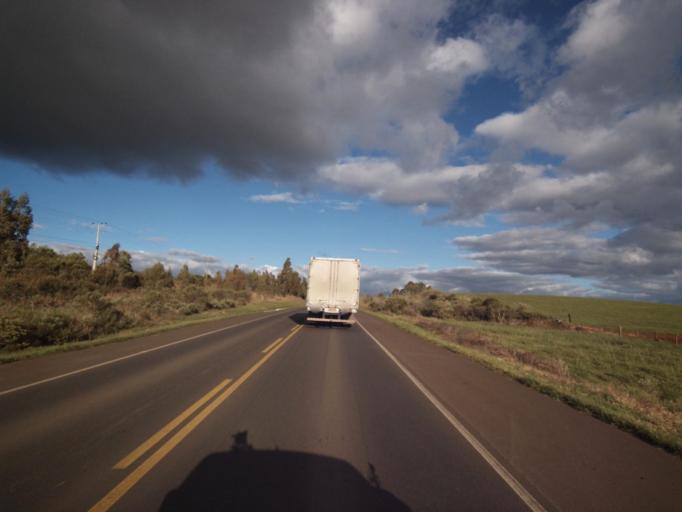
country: BR
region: Santa Catarina
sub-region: Campos Novos
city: Campos Novos
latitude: -27.3753
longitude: -51.2464
